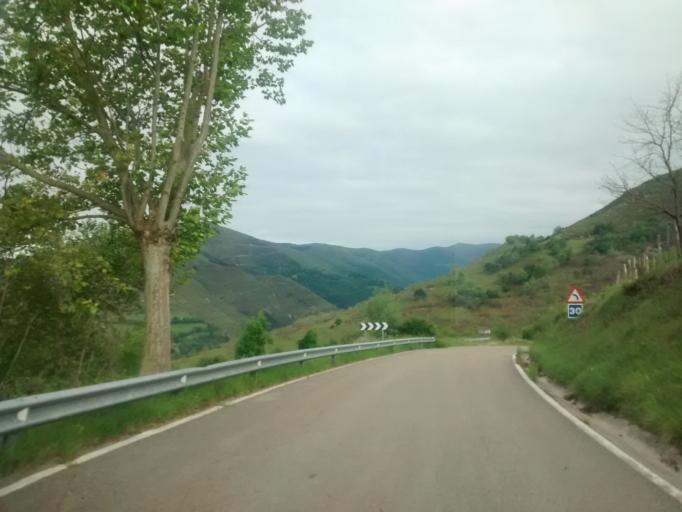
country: ES
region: Cantabria
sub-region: Provincia de Cantabria
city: San Vicente de la Barquera
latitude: 43.2510
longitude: -4.4273
